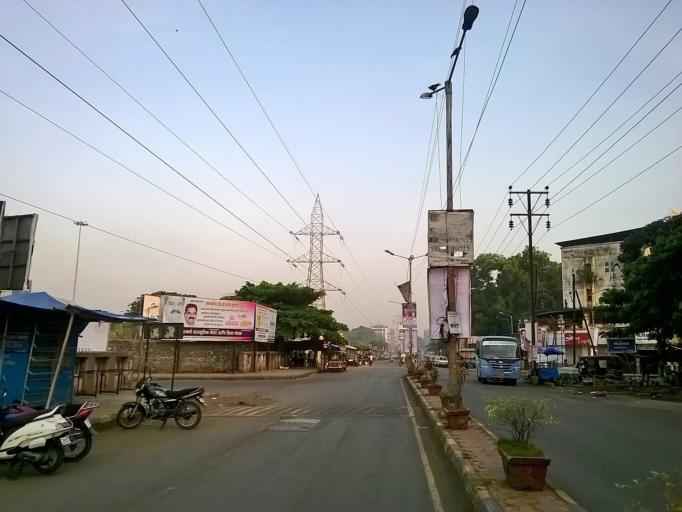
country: IN
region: Maharashtra
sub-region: Raigarh
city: Kalundri
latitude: 18.9916
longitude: 73.1231
